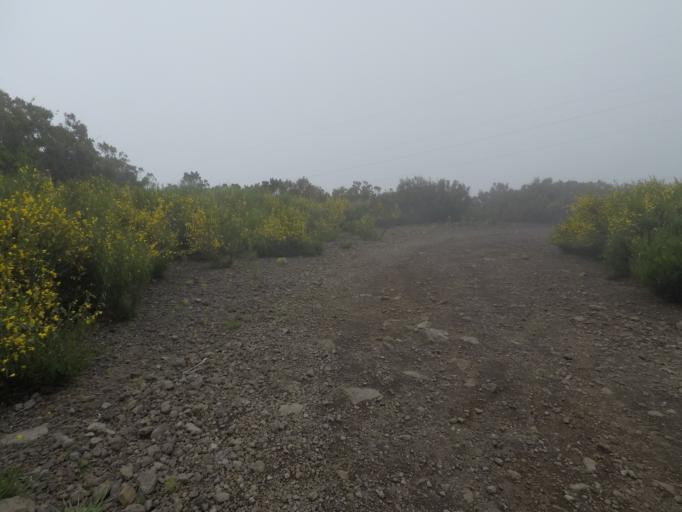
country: PT
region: Madeira
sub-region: Sao Vicente
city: Sao Vicente
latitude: 32.7744
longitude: -17.0649
